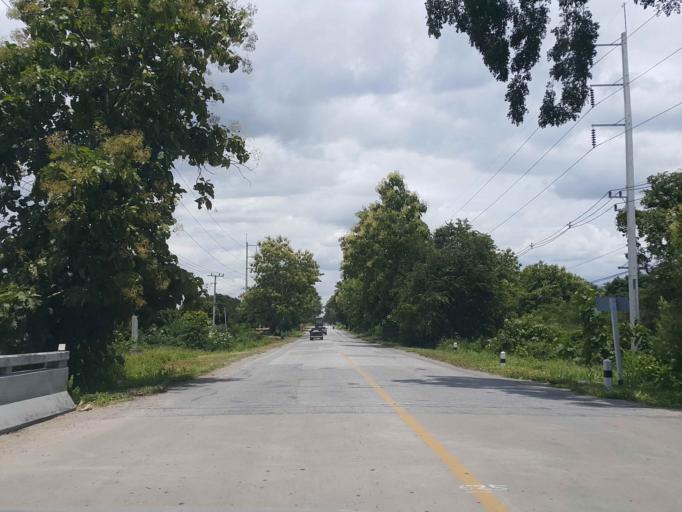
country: TH
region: Lamphun
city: Ban Hong
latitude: 18.3917
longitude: 98.8269
